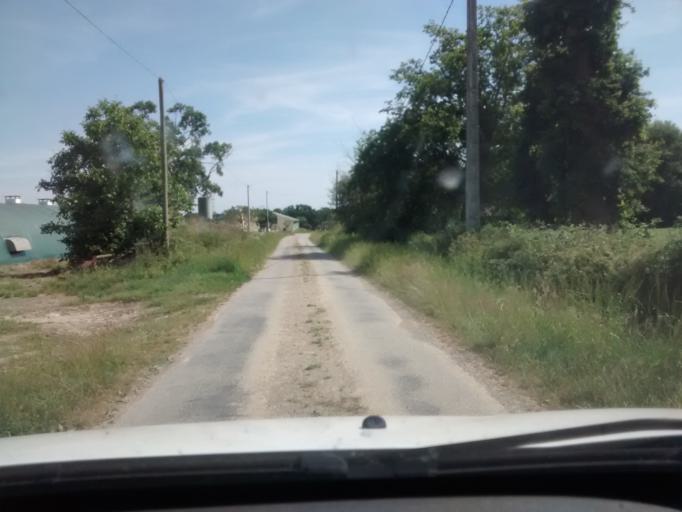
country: FR
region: Brittany
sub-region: Departement d'Ille-et-Vilaine
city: Cesson-Sevigne
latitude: 48.0955
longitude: -1.5705
